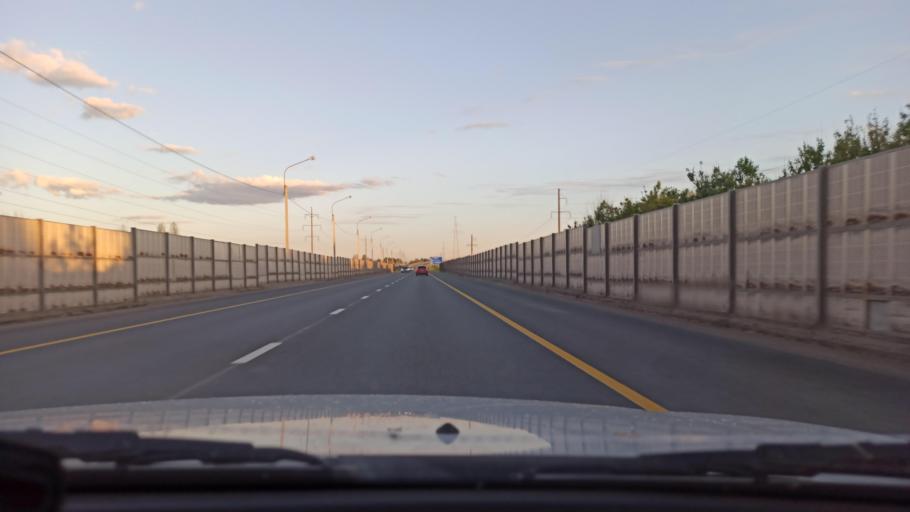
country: RU
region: Vologda
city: Vologda
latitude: 59.2250
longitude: 39.7747
